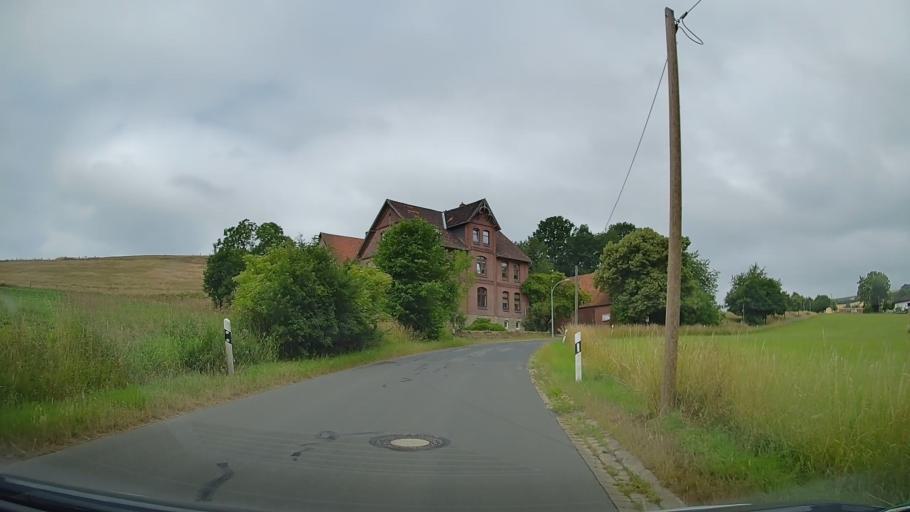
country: DE
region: Lower Saxony
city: Aerzen
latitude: 52.0477
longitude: 9.1897
